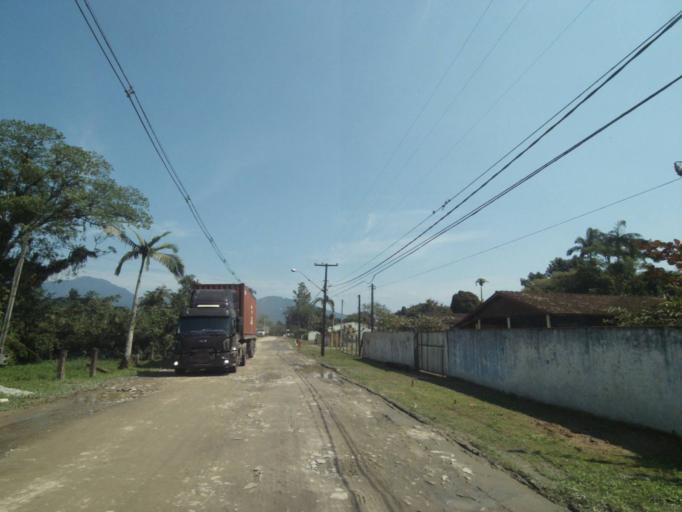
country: BR
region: Parana
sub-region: Paranagua
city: Paranagua
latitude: -25.5575
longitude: -48.6002
